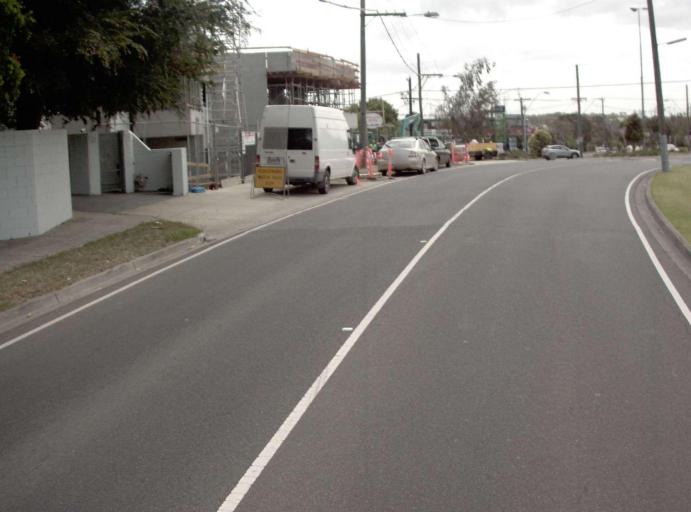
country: AU
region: Victoria
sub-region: Boroondara
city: Kew
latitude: -37.7957
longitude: 145.0372
